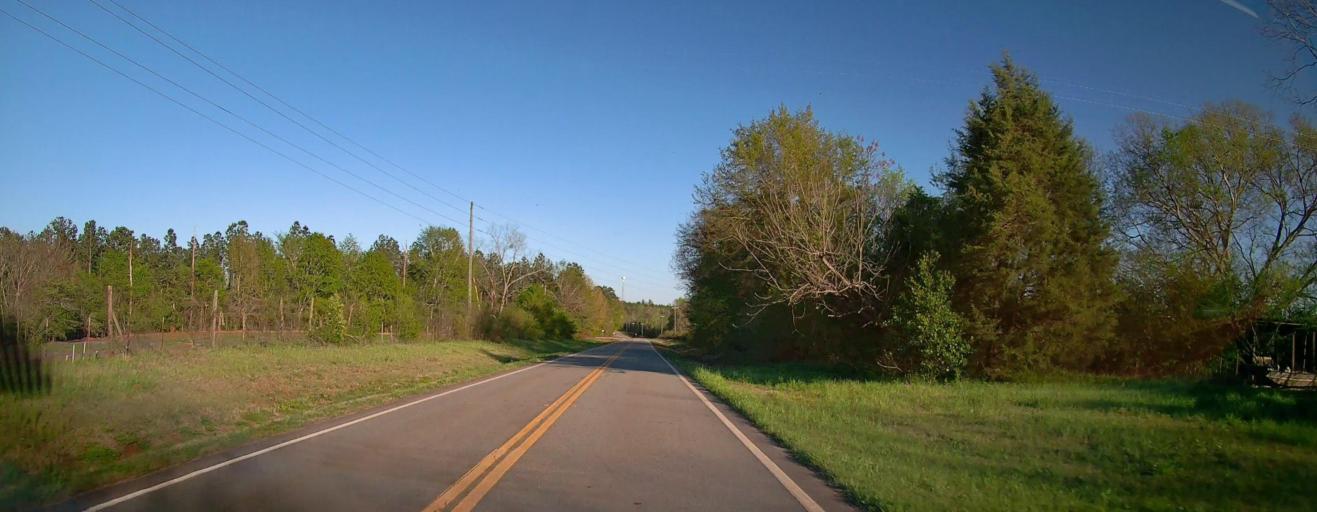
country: US
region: Georgia
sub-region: Wilkinson County
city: Irwinton
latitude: 32.8618
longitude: -83.0844
